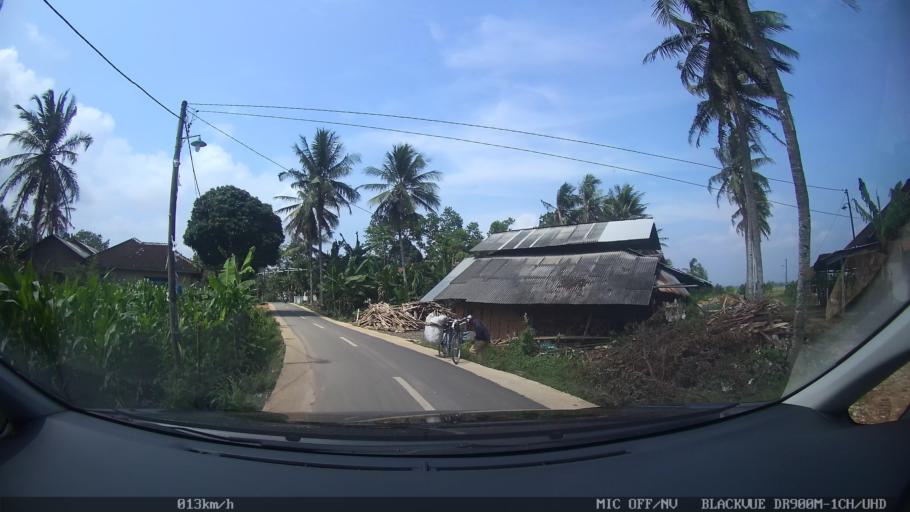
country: ID
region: Lampung
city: Kedaton
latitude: -5.3293
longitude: 105.2727
